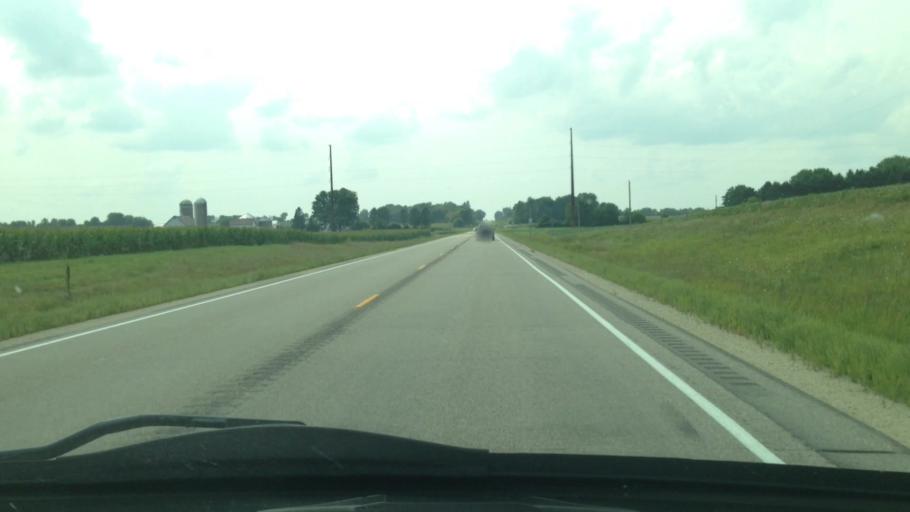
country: US
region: Minnesota
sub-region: Wabasha County
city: Elgin
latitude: 44.1658
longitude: -92.3740
